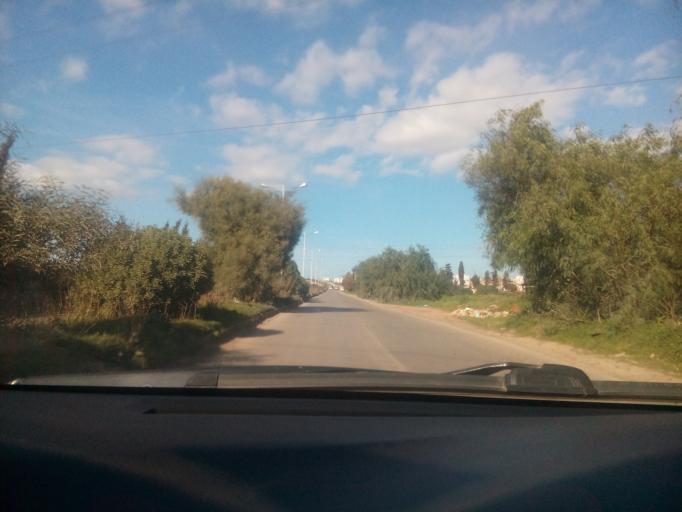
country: DZ
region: Oran
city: Bir el Djir
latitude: 35.6785
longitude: -0.5671
